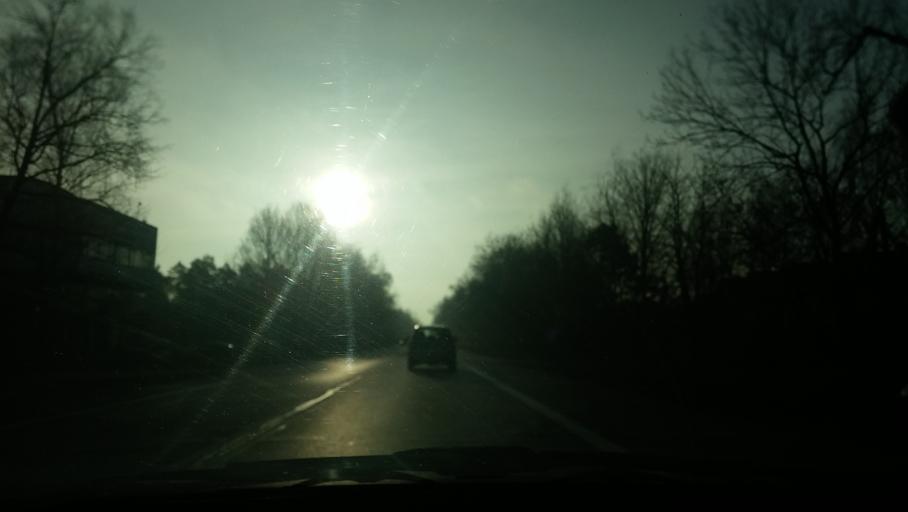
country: PL
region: Masovian Voivodeship
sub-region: Powiat minski
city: Sulejowek
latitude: 52.2211
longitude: 21.2513
